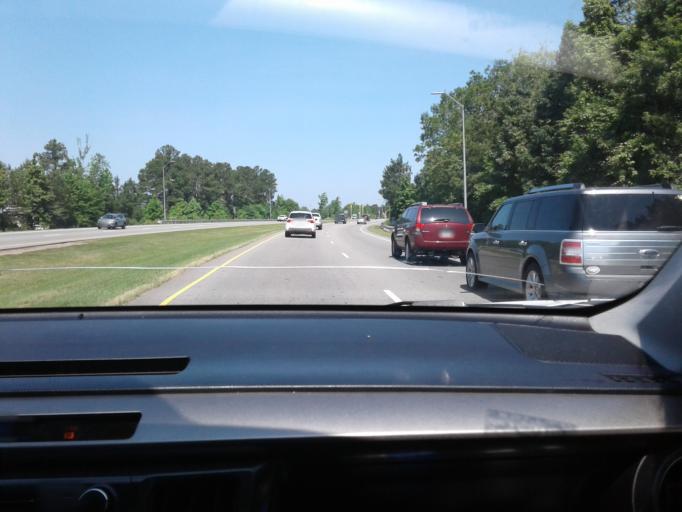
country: US
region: North Carolina
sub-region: Wake County
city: Holly Springs
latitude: 35.6401
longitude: -78.8346
